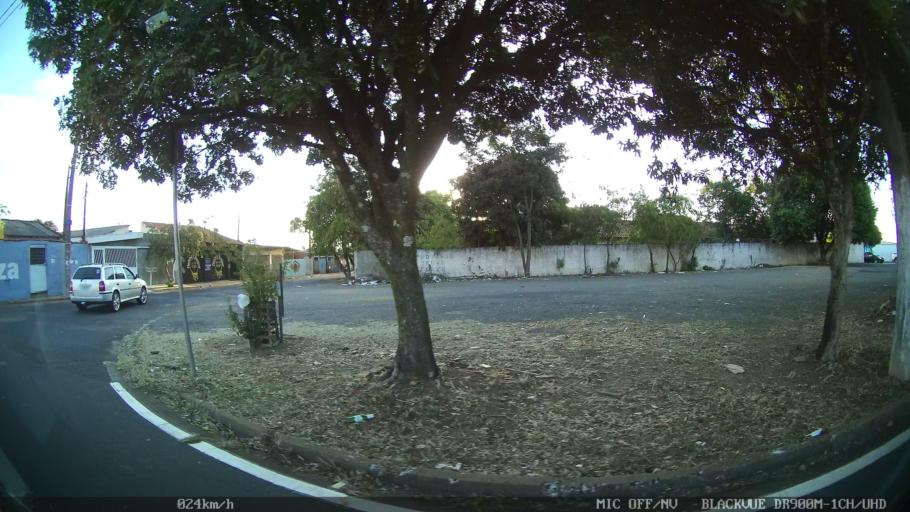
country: BR
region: Sao Paulo
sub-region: Franca
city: Franca
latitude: -20.5030
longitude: -47.4091
